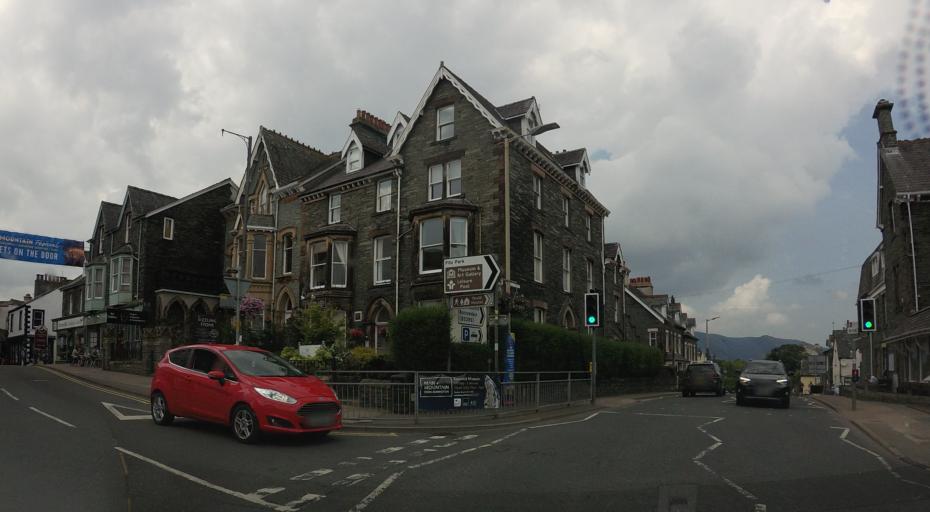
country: GB
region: England
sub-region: Cumbria
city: Keswick
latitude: 54.6012
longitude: -3.1346
